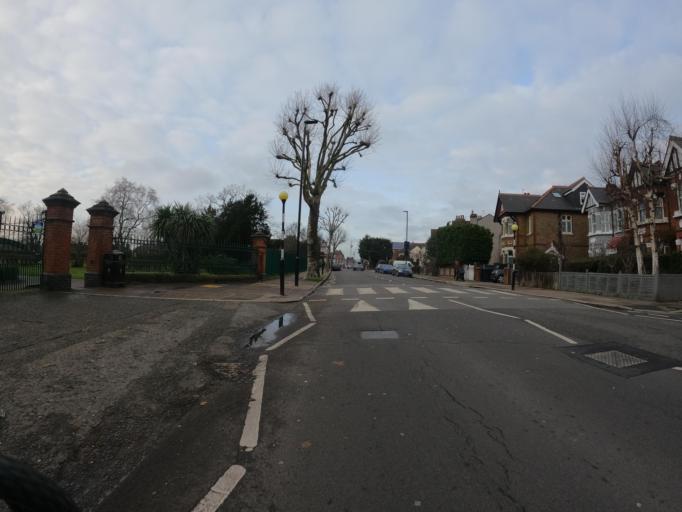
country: GB
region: England
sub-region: Greater London
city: Brentford
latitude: 51.5024
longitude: -0.3311
